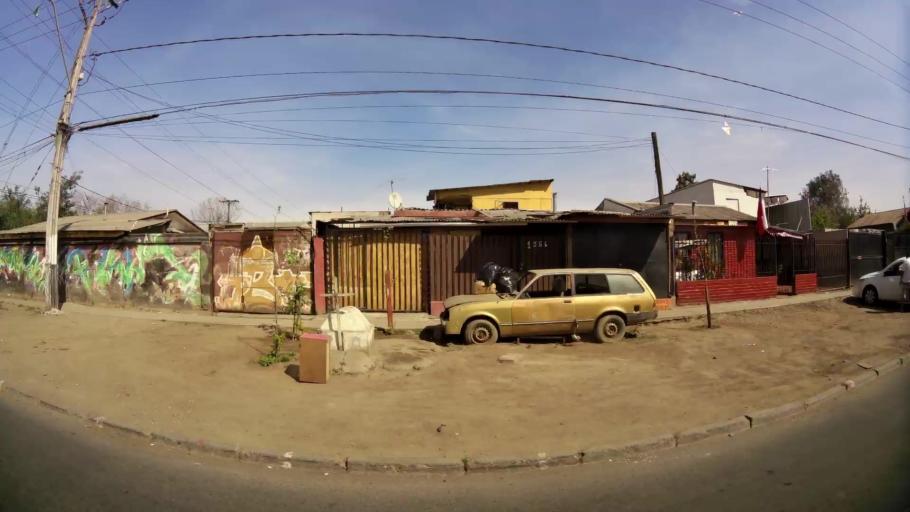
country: CL
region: Santiago Metropolitan
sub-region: Provincia de Santiago
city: Lo Prado
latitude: -33.4216
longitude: -70.7476
